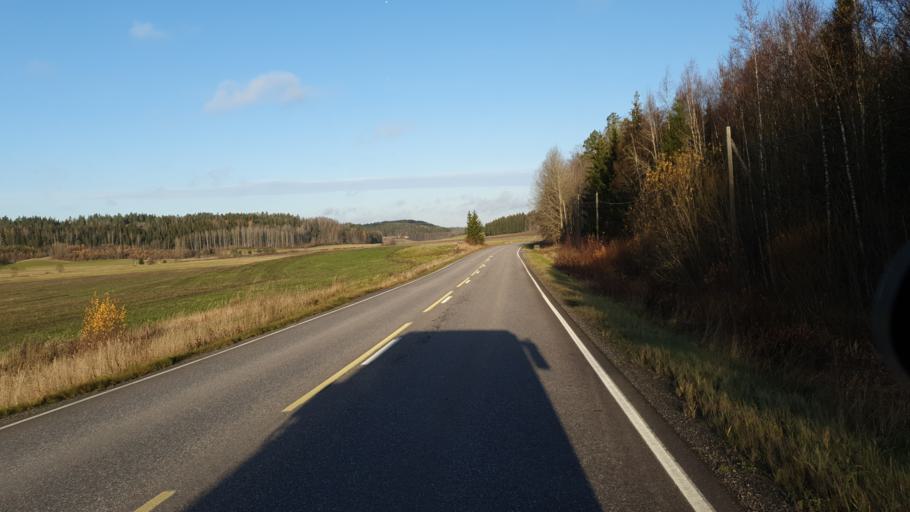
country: FI
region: Uusimaa
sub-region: Helsinki
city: Siuntio
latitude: 60.2071
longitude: 24.1829
